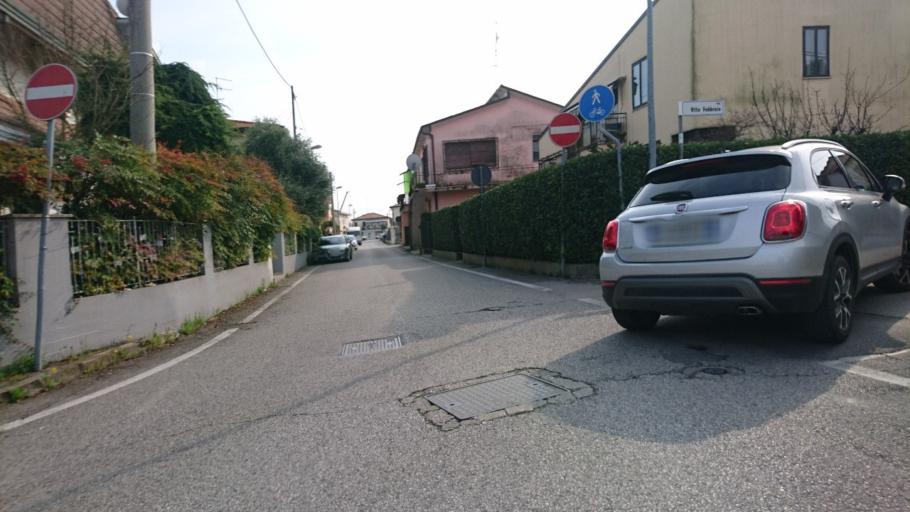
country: IT
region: Veneto
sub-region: Provincia di Padova
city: San Vito
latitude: 45.4293
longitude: 11.9580
